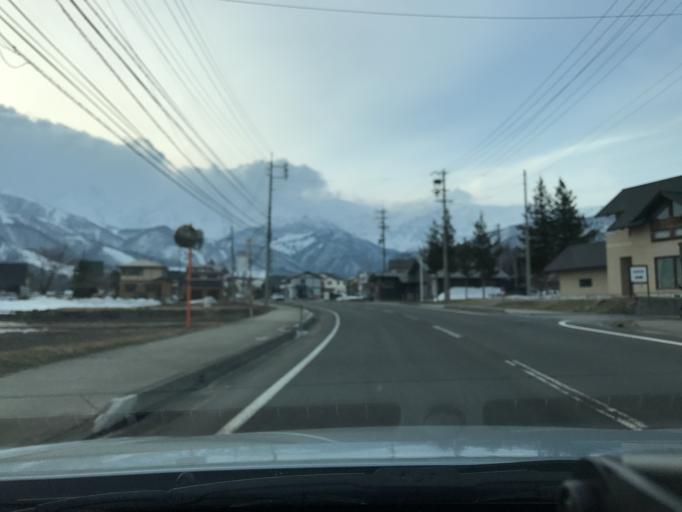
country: JP
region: Nagano
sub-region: Kitaazumi Gun
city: Hakuba
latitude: 36.6981
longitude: 137.8572
